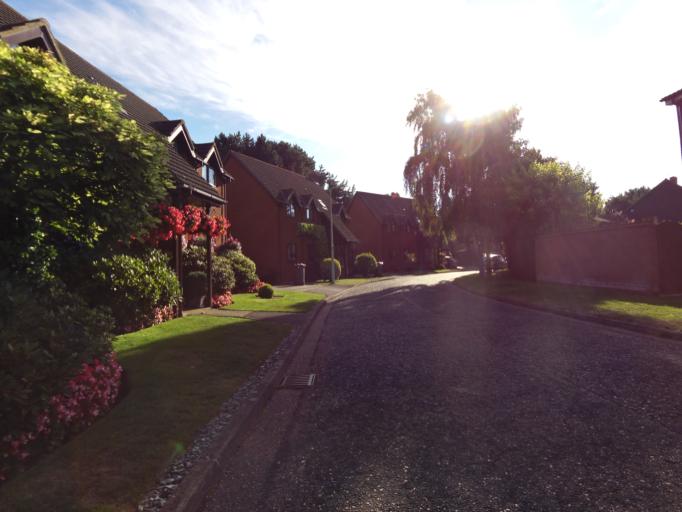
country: GB
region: England
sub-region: Suffolk
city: Kesgrave
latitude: 52.0650
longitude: 1.2675
